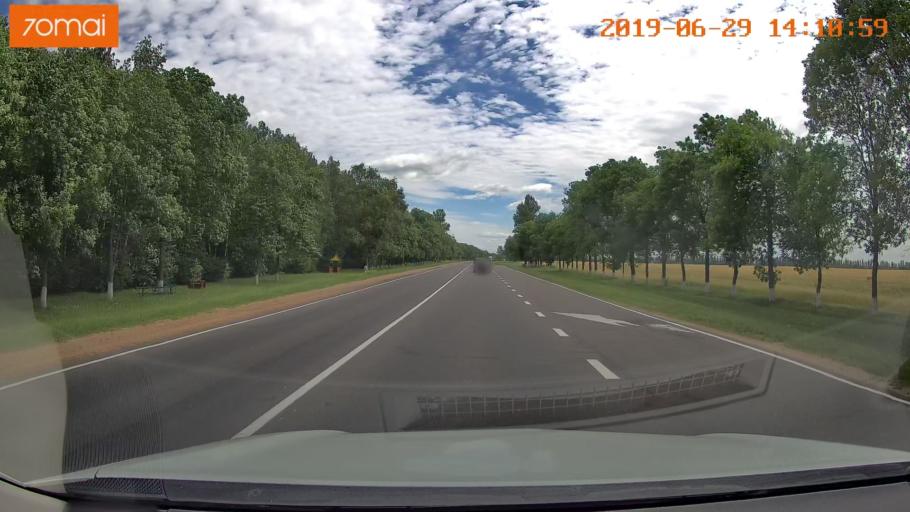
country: BY
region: Minsk
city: Salihorsk
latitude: 52.8242
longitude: 27.4993
